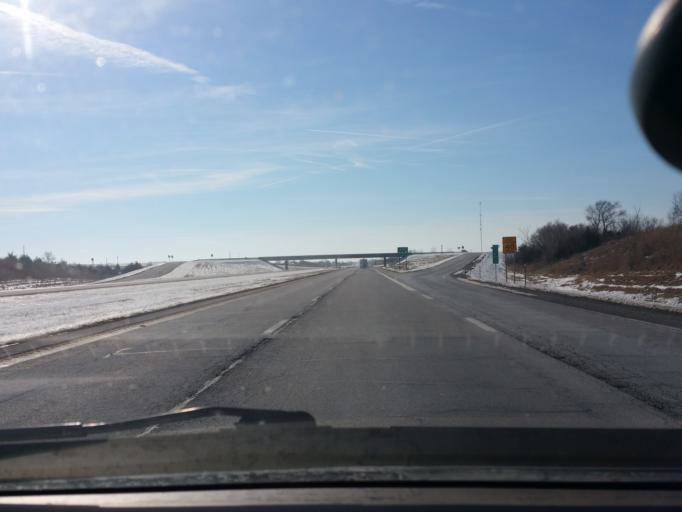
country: US
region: Missouri
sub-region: Harrison County
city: Bethany
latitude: 40.3781
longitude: -94.0021
